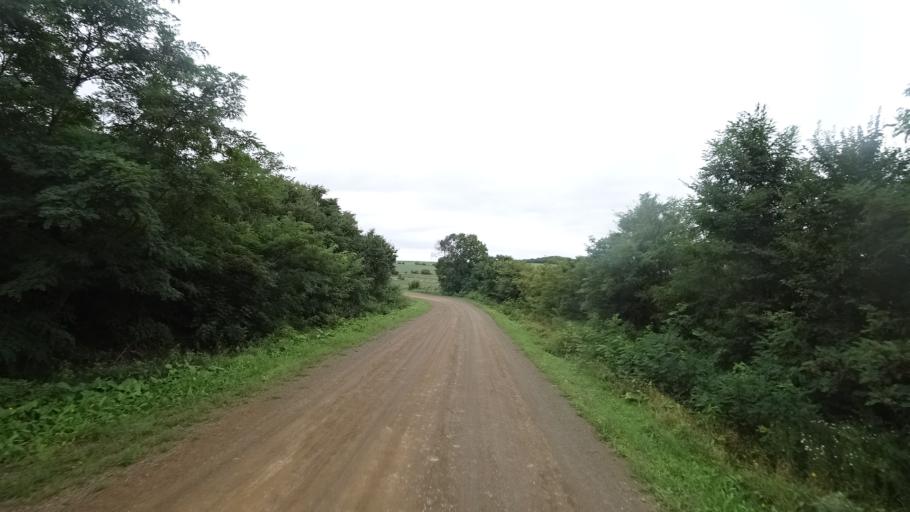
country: RU
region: Primorskiy
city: Chernigovka
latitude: 44.4538
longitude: 132.5838
